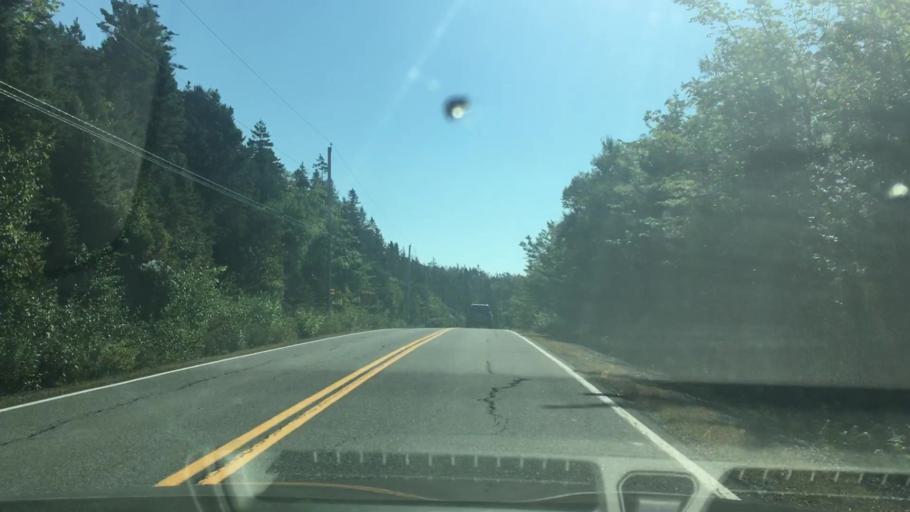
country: CA
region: Nova Scotia
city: Cole Harbour
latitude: 44.8124
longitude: -62.8392
